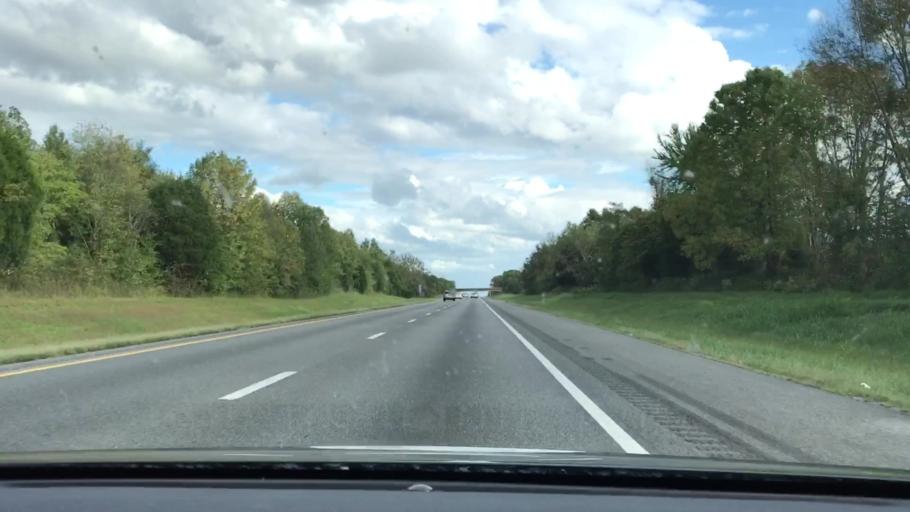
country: US
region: Tennessee
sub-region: Cheatham County
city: Pleasant View
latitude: 36.4805
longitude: -87.1492
